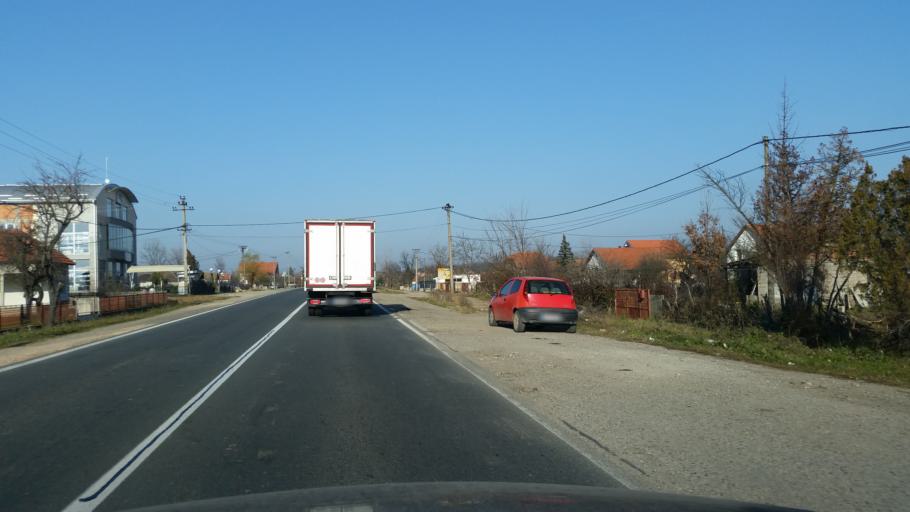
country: RS
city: Stepojevac
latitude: 44.5356
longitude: 20.2987
